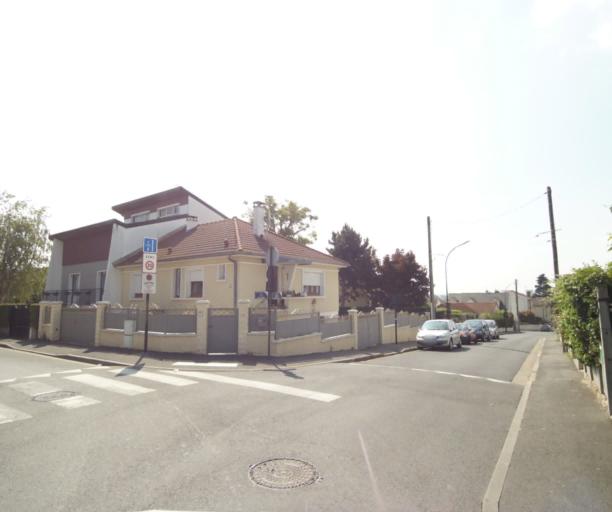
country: FR
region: Ile-de-France
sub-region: Departement du Val-d'Oise
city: Sannois
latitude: 48.9592
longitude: 2.2445
